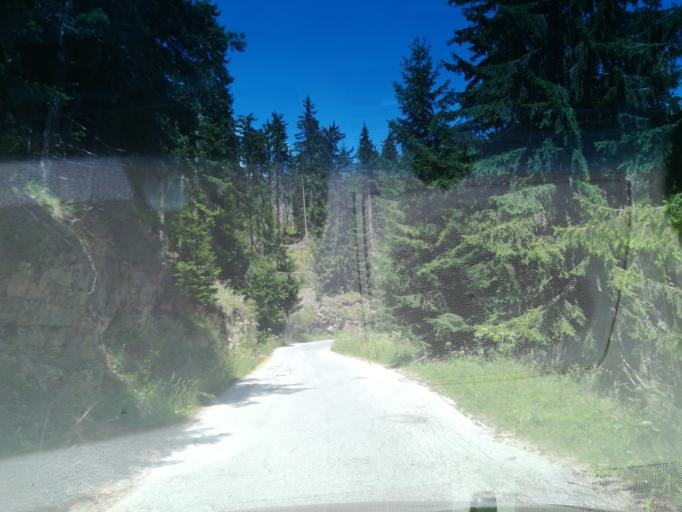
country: BG
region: Smolyan
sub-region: Obshtina Chepelare
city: Chepelare
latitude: 41.6913
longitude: 24.7707
